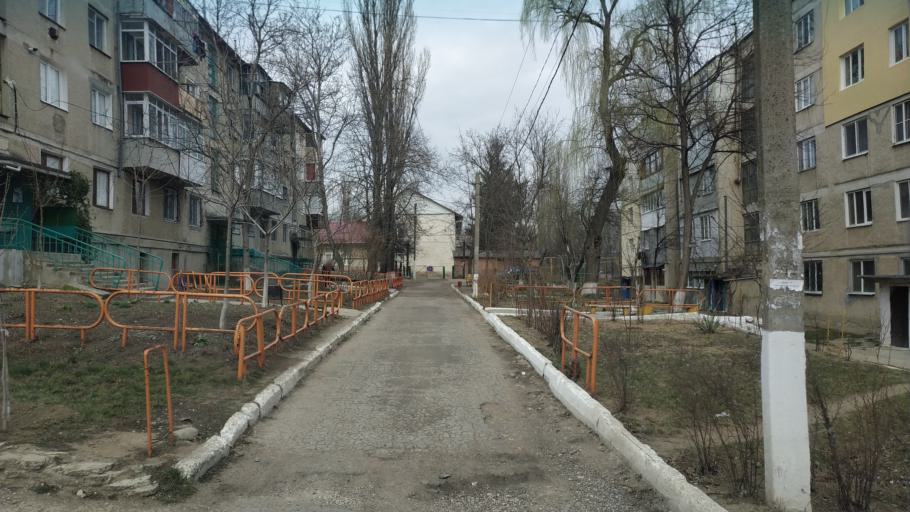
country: MD
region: Chisinau
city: Singera
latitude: 46.9354
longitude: 28.9787
